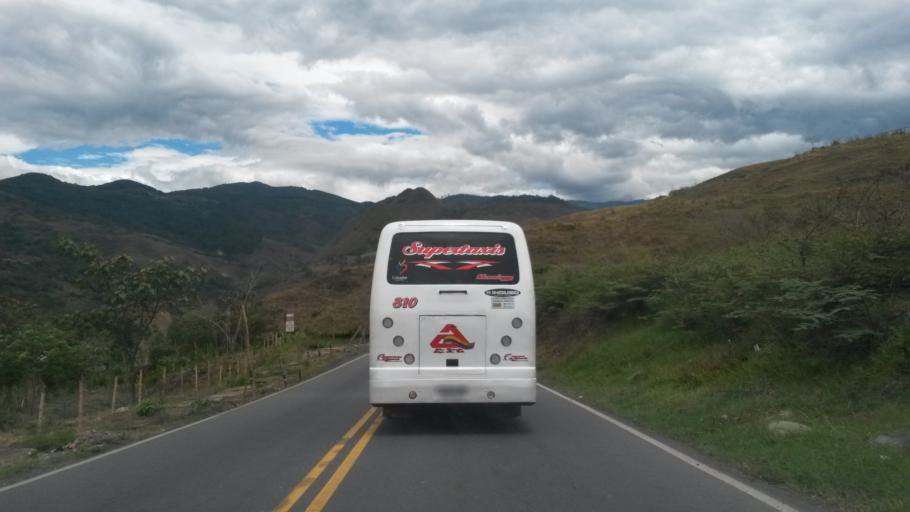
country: CO
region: Cauca
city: Rosas
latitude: 2.2816
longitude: -76.7194
